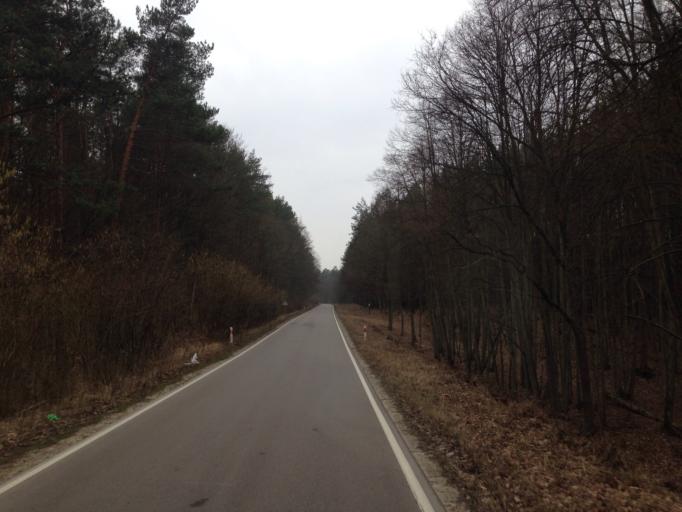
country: PL
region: Pomeranian Voivodeship
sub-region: Powiat starogardzki
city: Smetowo Graniczne
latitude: 53.7515
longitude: 18.7773
